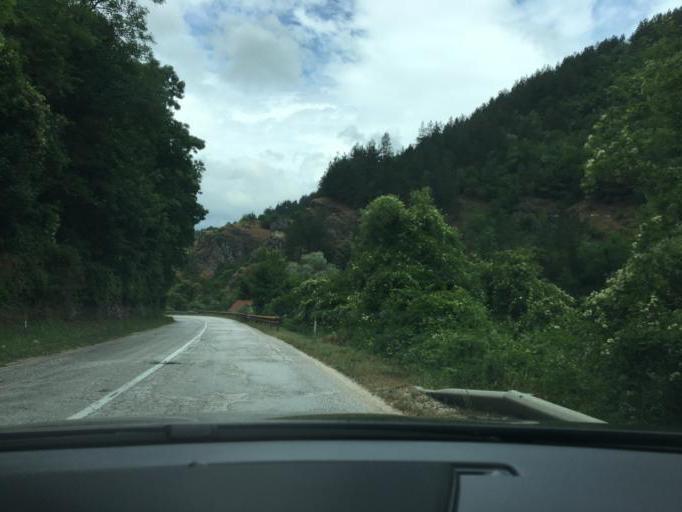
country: MK
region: Kriva Palanka
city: Kriva Palanka
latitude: 42.2287
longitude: 22.3805
